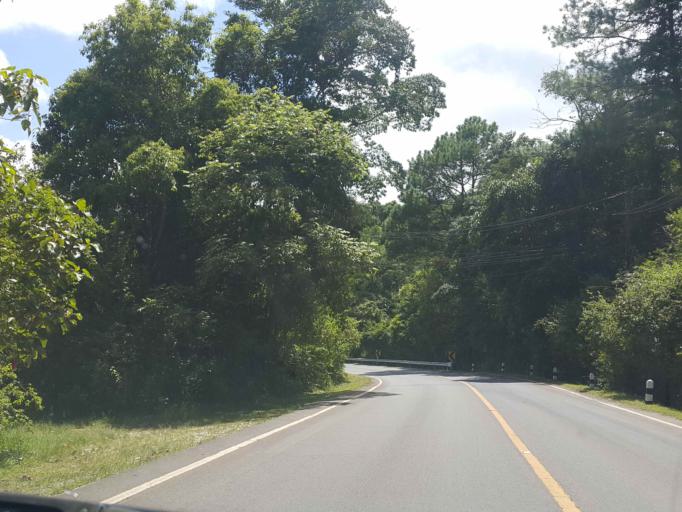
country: TH
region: Chiang Mai
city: Chom Thong
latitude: 18.5432
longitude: 98.5587
